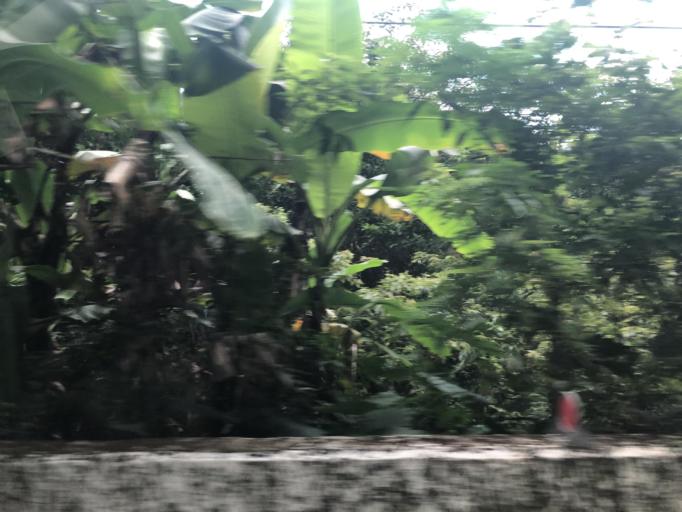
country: TW
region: Taipei
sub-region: Taipei
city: Banqiao
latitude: 24.8942
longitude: 121.4255
